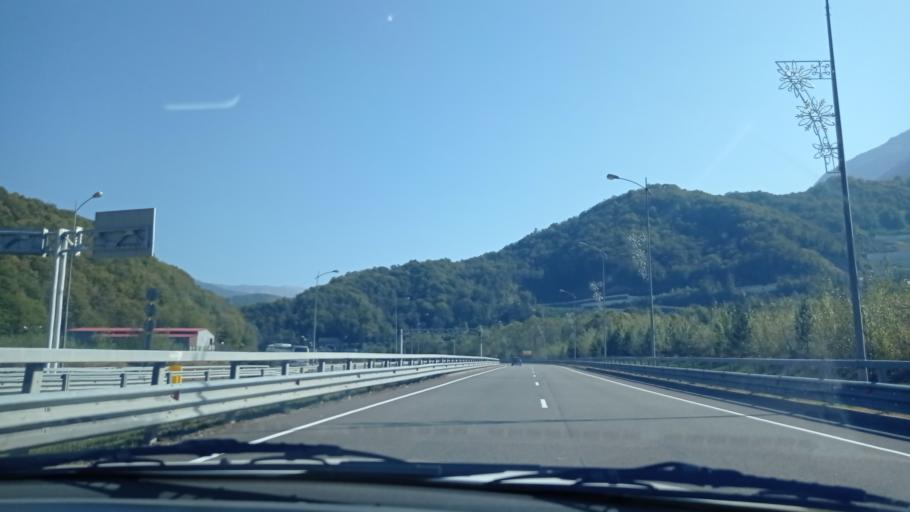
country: RU
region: Krasnodarskiy
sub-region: Sochi City
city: Krasnaya Polyana
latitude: 43.6860
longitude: 40.2356
